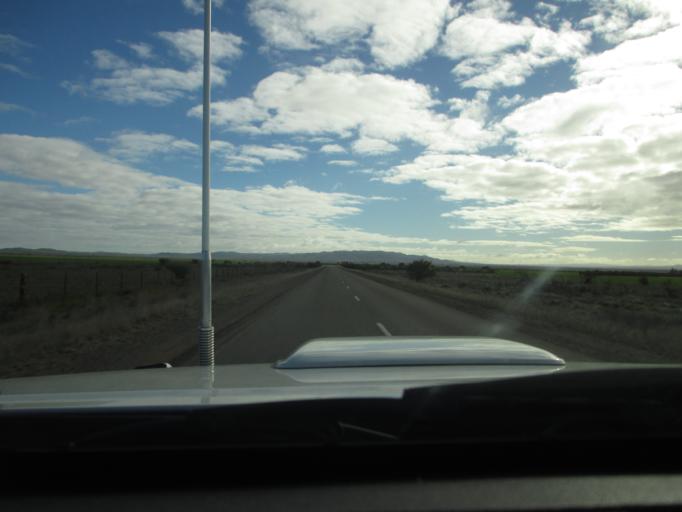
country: AU
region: South Australia
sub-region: Peterborough
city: Peterborough
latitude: -32.7002
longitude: 138.6099
